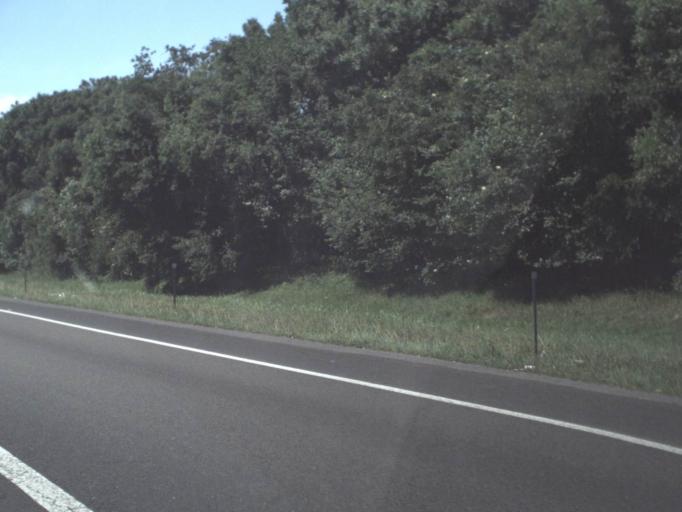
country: US
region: Florida
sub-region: Clay County
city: Bellair-Meadowbrook Terrace
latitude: 30.2516
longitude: -81.7631
